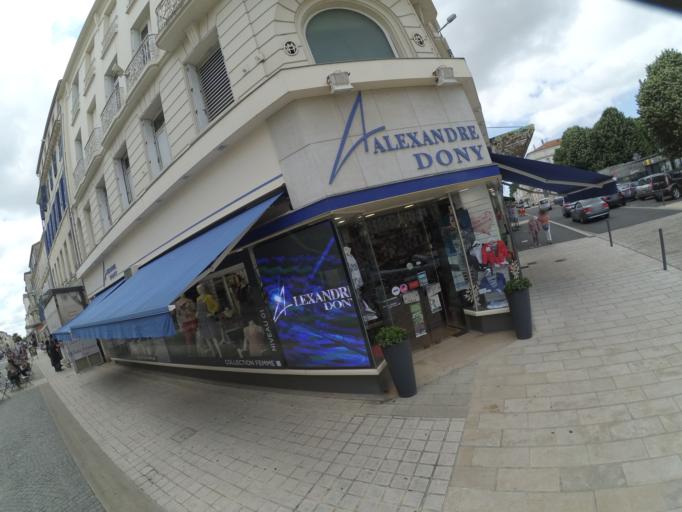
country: FR
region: Poitou-Charentes
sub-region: Departement de la Charente-Maritime
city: Rochefort
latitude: 45.9360
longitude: -0.9613
